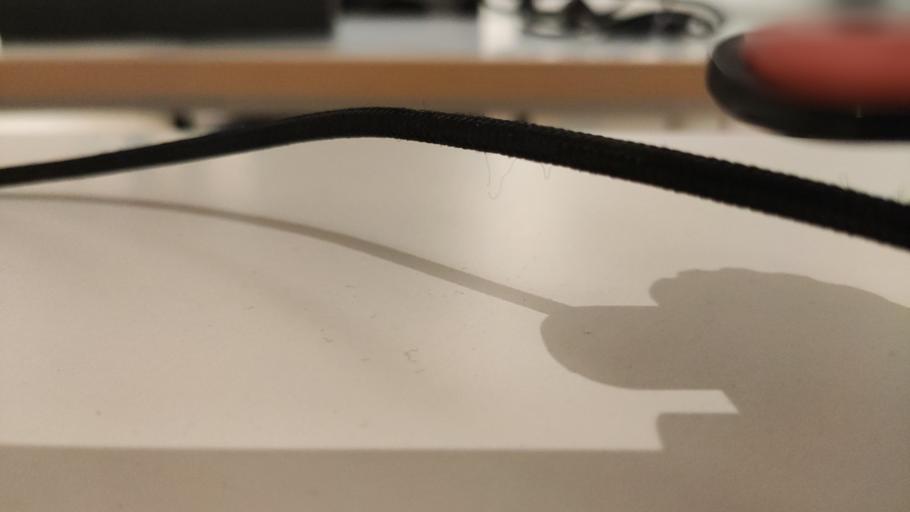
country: RU
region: Kaluga
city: Borovsk
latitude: 55.3688
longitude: 36.4133
